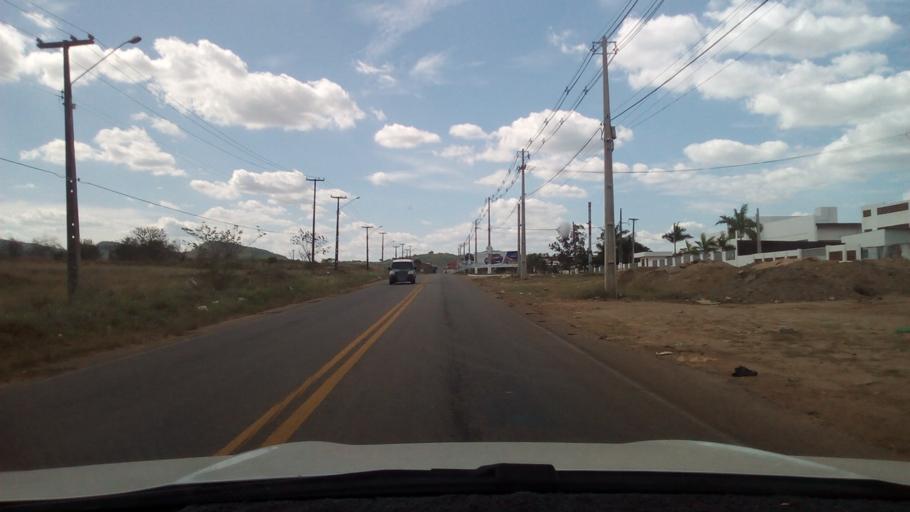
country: BR
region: Paraiba
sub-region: Guarabira
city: Guarabira
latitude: -6.8741
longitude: -35.4820
